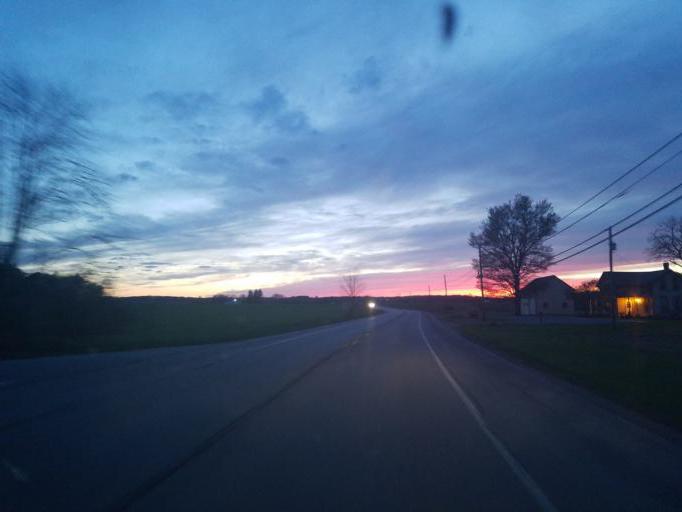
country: US
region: Ohio
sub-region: Wayne County
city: Apple Creek
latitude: 40.7556
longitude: -81.8505
